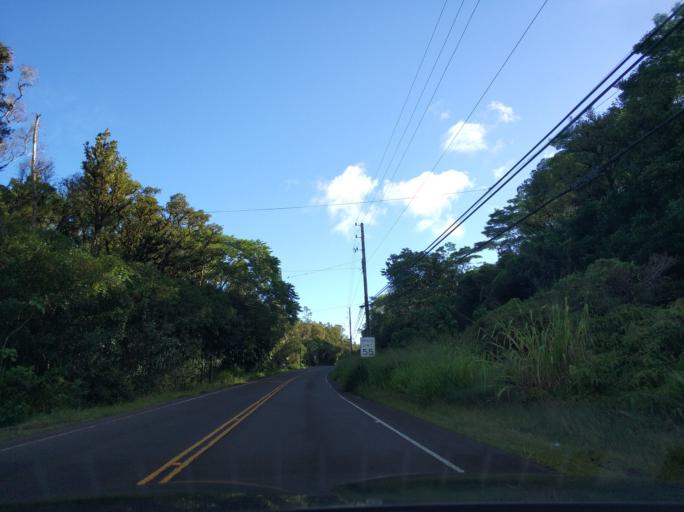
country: US
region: Hawaii
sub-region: Hawaii County
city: Leilani Estates
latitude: 19.4611
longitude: -154.9409
